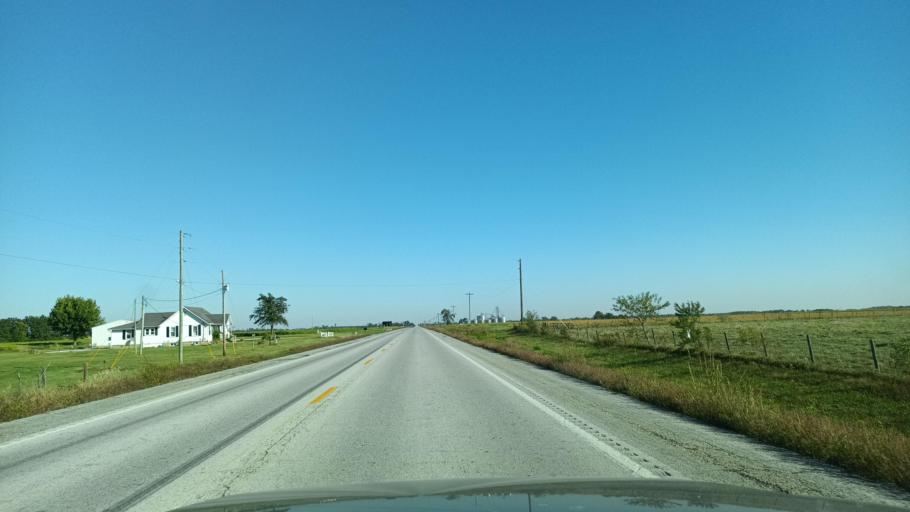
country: US
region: Missouri
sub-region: Audrain County
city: Vandalia
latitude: 39.3557
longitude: -91.6426
